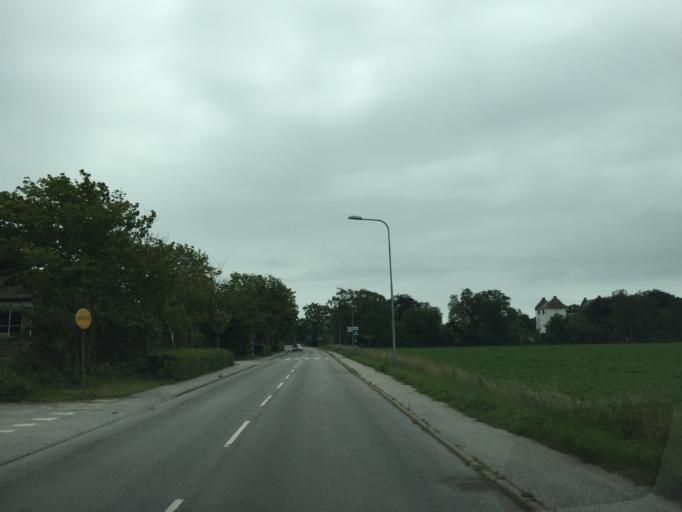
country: SE
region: Skane
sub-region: Ystads Kommun
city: Kopingebro
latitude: 55.4307
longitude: 14.1131
